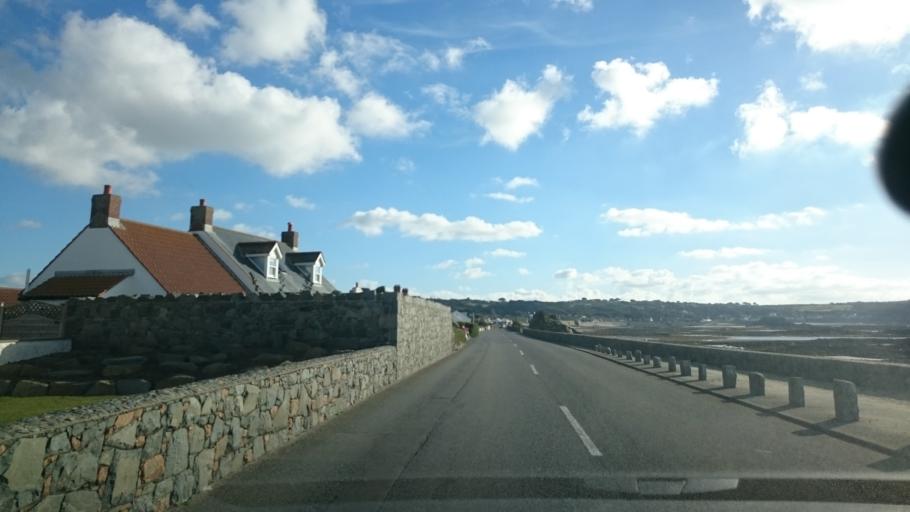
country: GG
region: St Peter Port
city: Saint Peter Port
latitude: 49.4512
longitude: -2.6499
